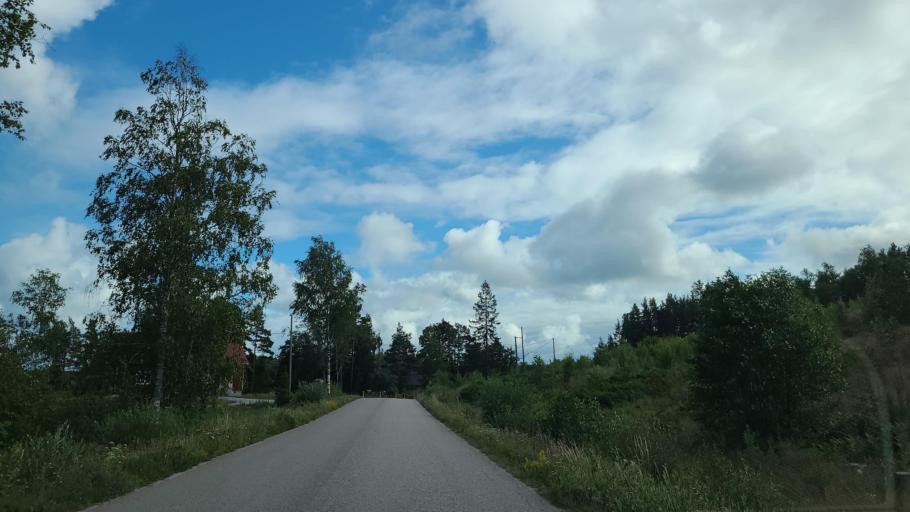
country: FI
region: Varsinais-Suomi
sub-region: Aboland-Turunmaa
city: Nagu
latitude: 60.1583
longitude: 21.7553
